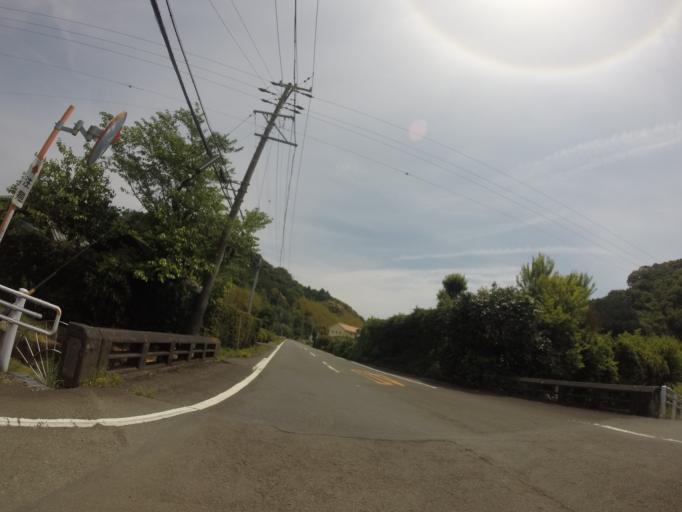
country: JP
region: Shizuoka
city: Fujieda
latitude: 34.9128
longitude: 138.2437
